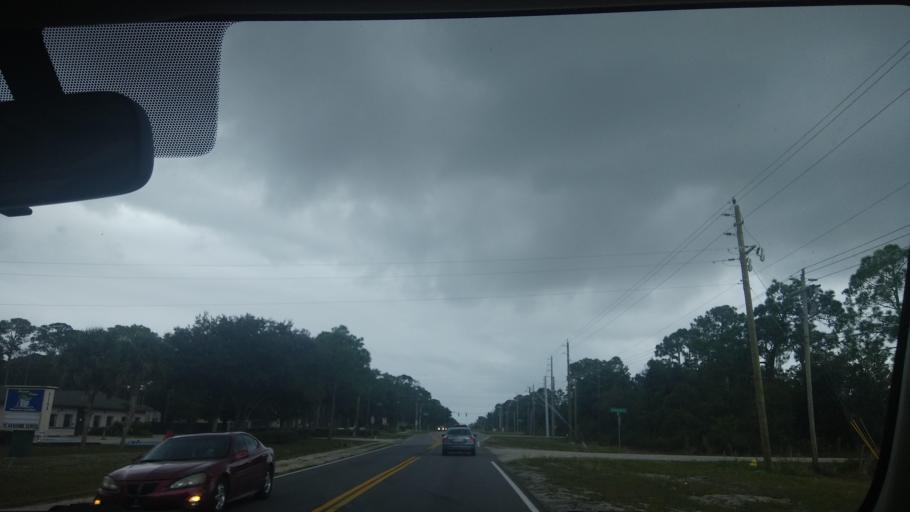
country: US
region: Florida
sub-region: Brevard County
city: Grant-Valkaria
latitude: 27.9682
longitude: -80.6226
